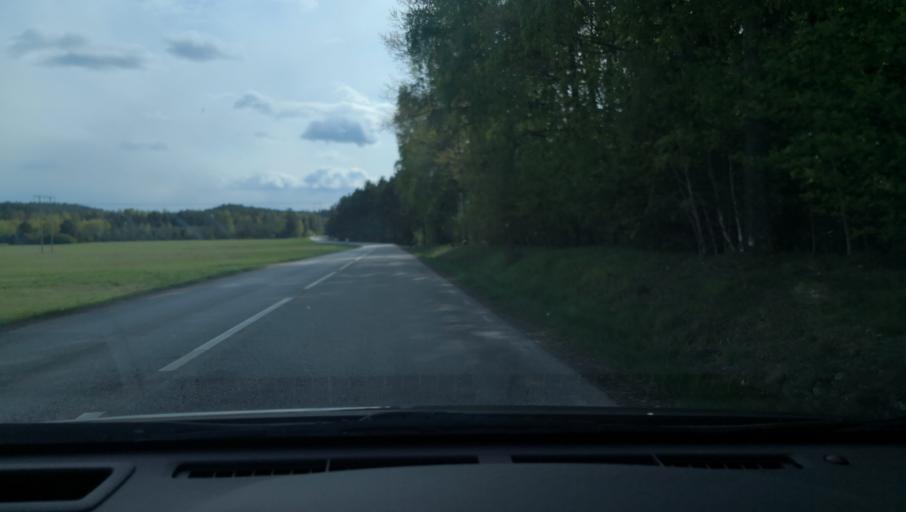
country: SE
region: OErebro
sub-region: Askersunds Kommun
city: Asbro
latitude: 59.0520
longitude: 15.0491
